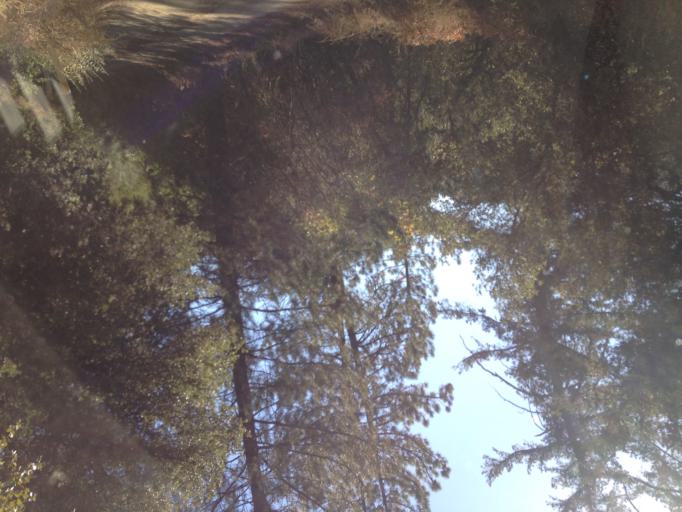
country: US
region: California
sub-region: San Bernardino County
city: Running Springs
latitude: 34.1666
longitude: -117.0739
